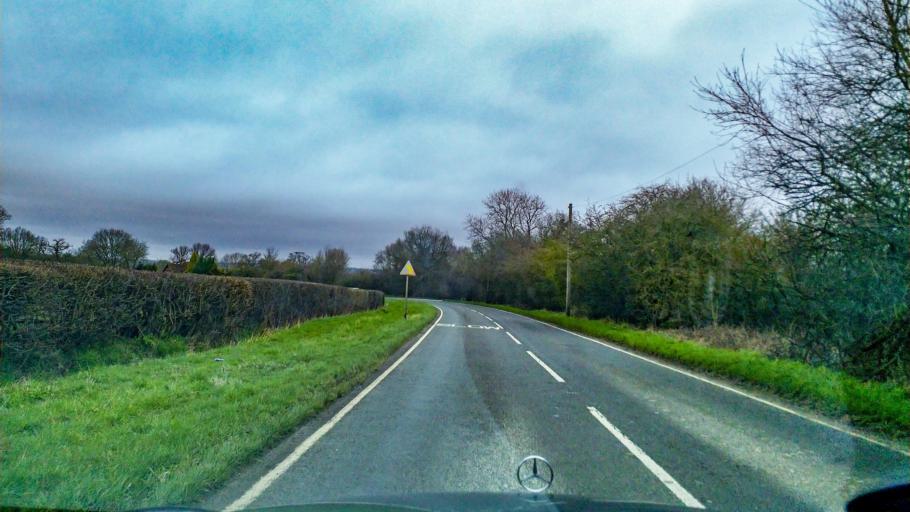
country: GB
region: England
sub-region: Surrey
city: Reigate
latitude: 51.2025
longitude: -0.2447
